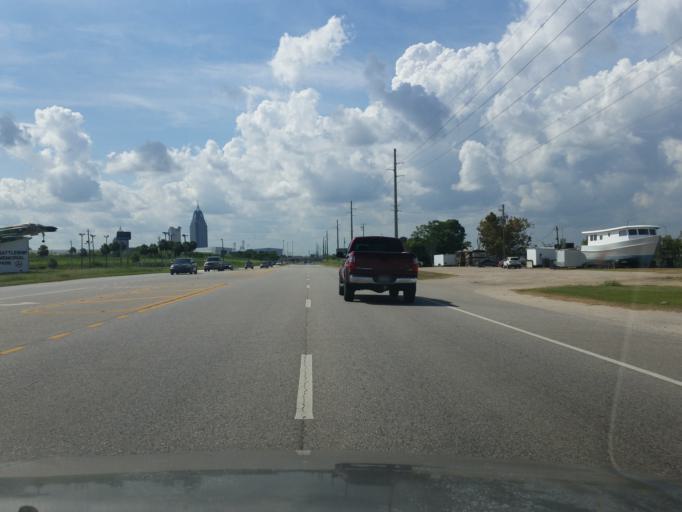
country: US
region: Alabama
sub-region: Mobile County
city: Mobile
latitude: 30.6868
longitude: -88.0144
